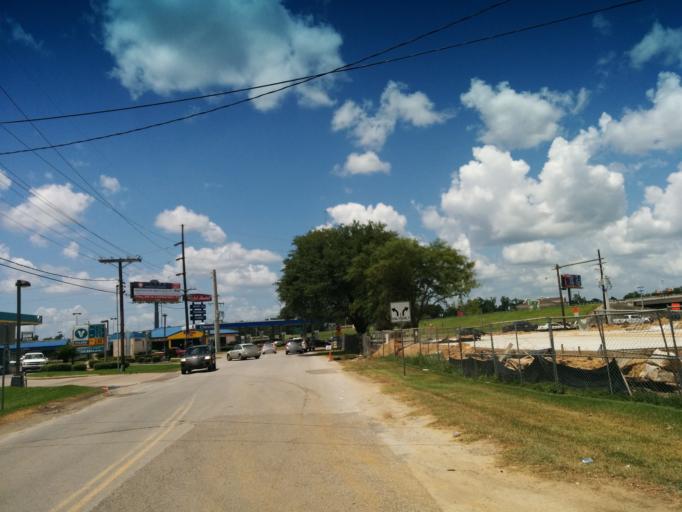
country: US
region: Texas
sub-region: Jefferson County
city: Beaumont
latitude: 30.1325
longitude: -94.1690
